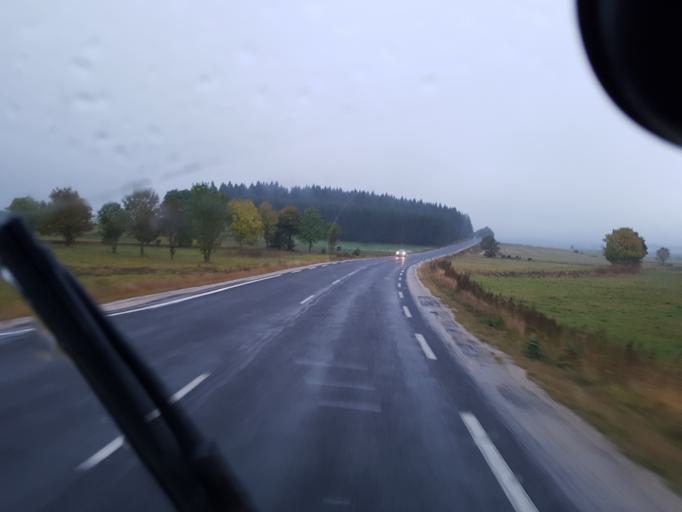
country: FR
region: Languedoc-Roussillon
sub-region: Departement de la Lozere
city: Langogne
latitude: 44.8248
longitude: 3.8714
